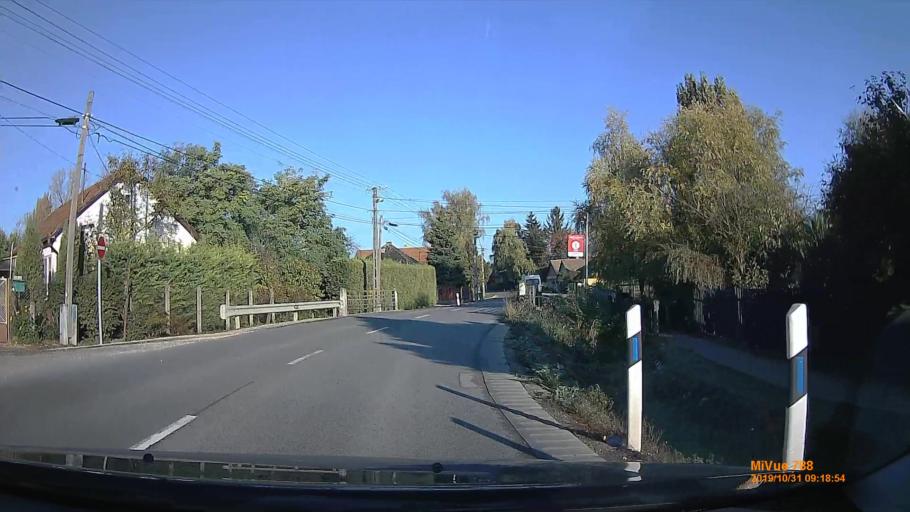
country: HU
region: Pest
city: Gyomro
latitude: 47.4147
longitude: 19.3948
